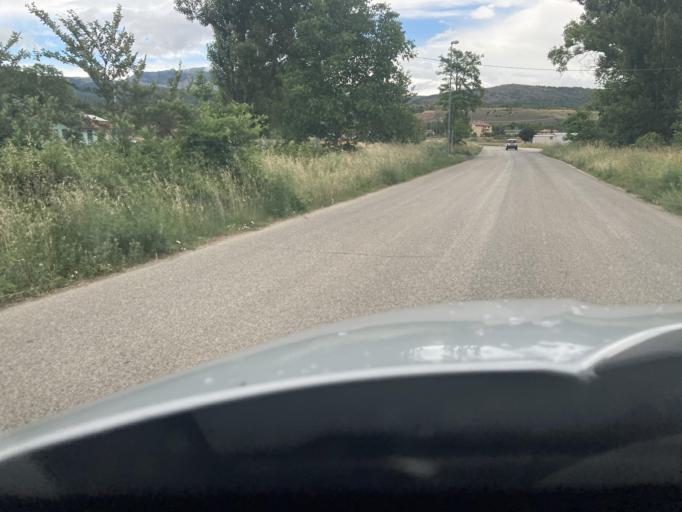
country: IT
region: Abruzzo
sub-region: Provincia dell' Aquila
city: Sant'Eusanio Forconese
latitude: 42.2938
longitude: 13.5310
